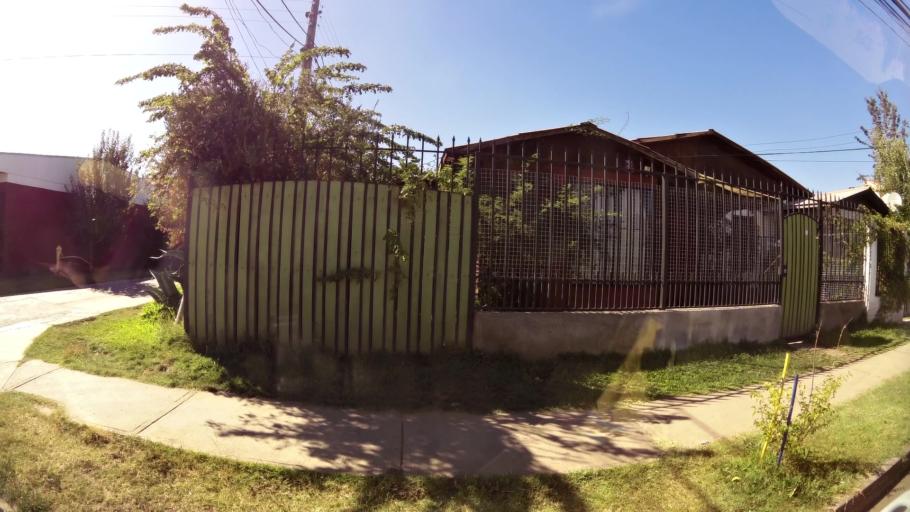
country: CL
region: O'Higgins
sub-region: Provincia de Cachapoal
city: Rancagua
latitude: -34.1771
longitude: -70.7042
